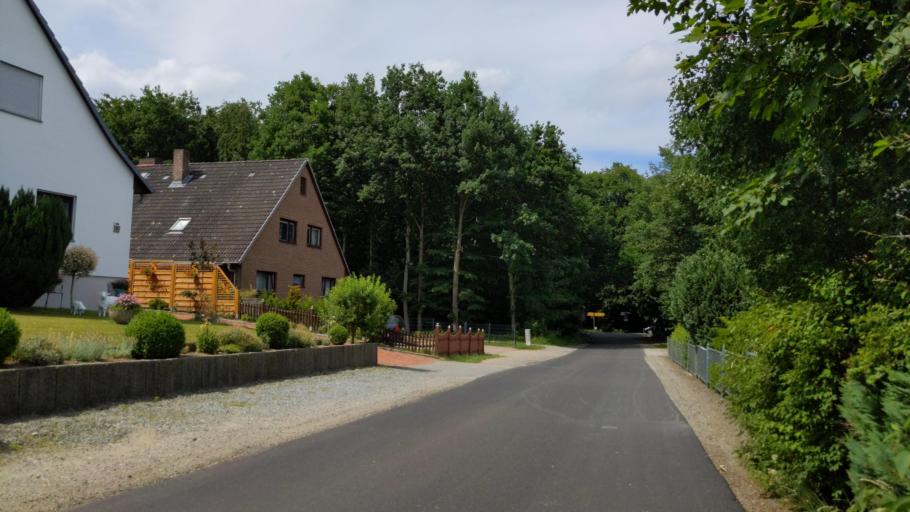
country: DE
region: Schleswig-Holstein
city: Kasseedorf
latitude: 54.1460
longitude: 10.6866
